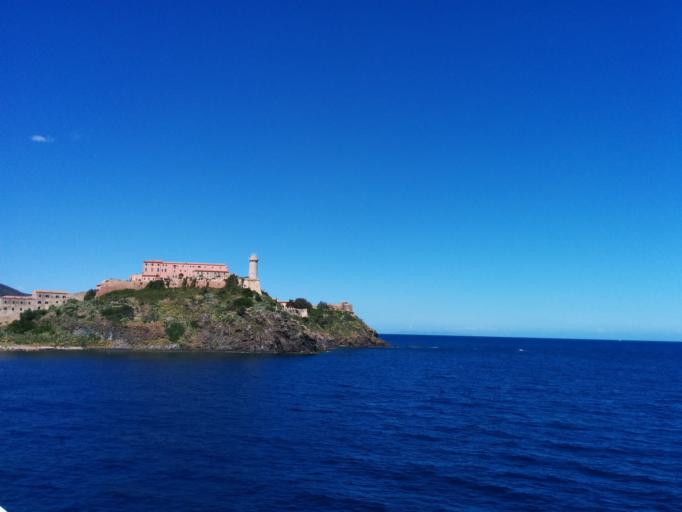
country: IT
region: Tuscany
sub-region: Provincia di Livorno
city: Portoferraio
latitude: 42.8154
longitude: 10.3389
